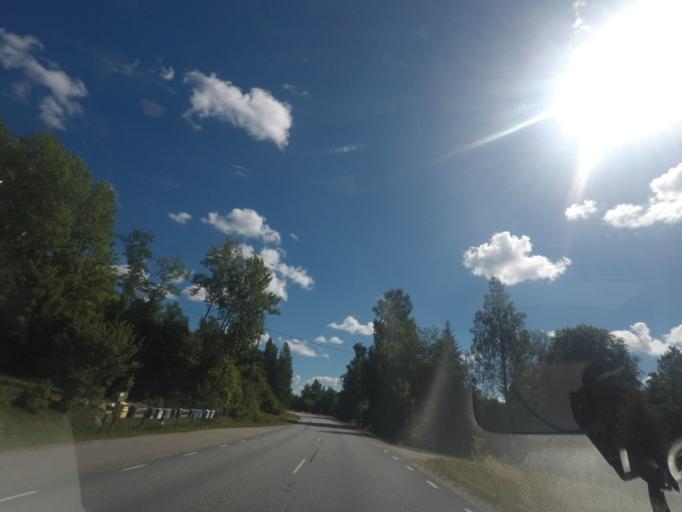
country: SE
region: Stockholm
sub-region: Norrtalje Kommun
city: Skanninge
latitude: 59.8942
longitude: 18.4569
